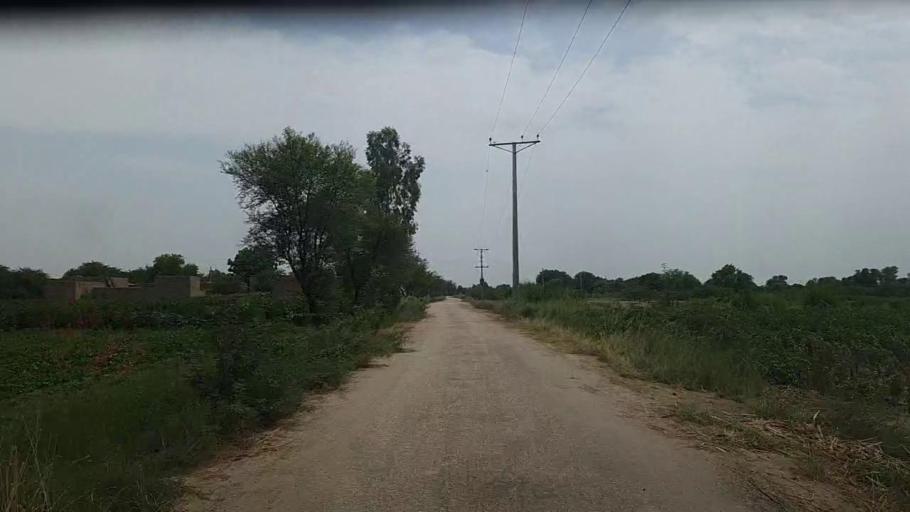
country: PK
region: Sindh
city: Bhiria
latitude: 26.8814
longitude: 68.2953
